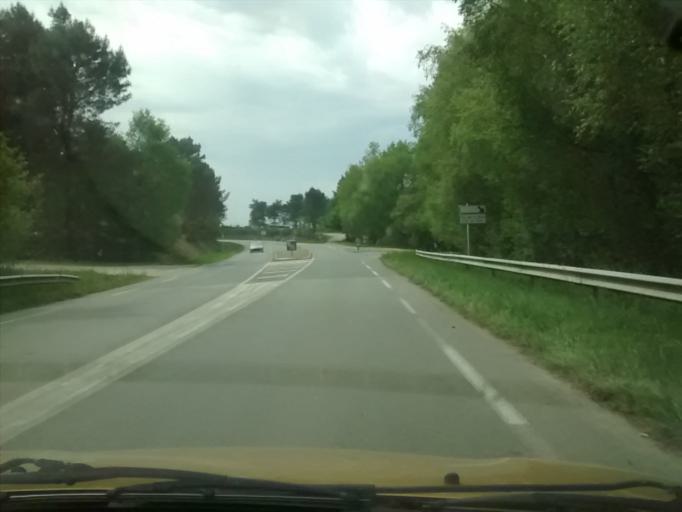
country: FR
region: Brittany
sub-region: Departement du Morbihan
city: Berric
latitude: 47.6028
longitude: -2.5471
